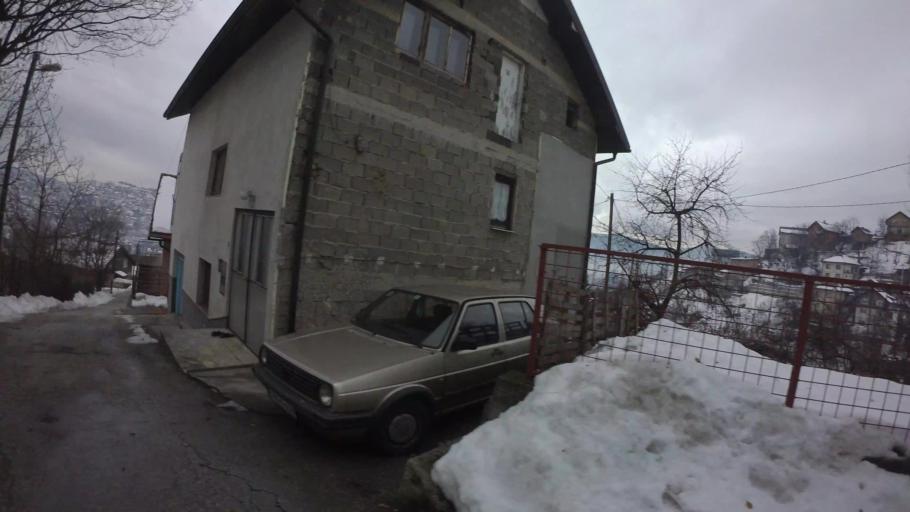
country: BA
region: Federation of Bosnia and Herzegovina
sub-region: Kanton Sarajevo
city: Sarajevo
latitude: 43.8546
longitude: 18.3548
